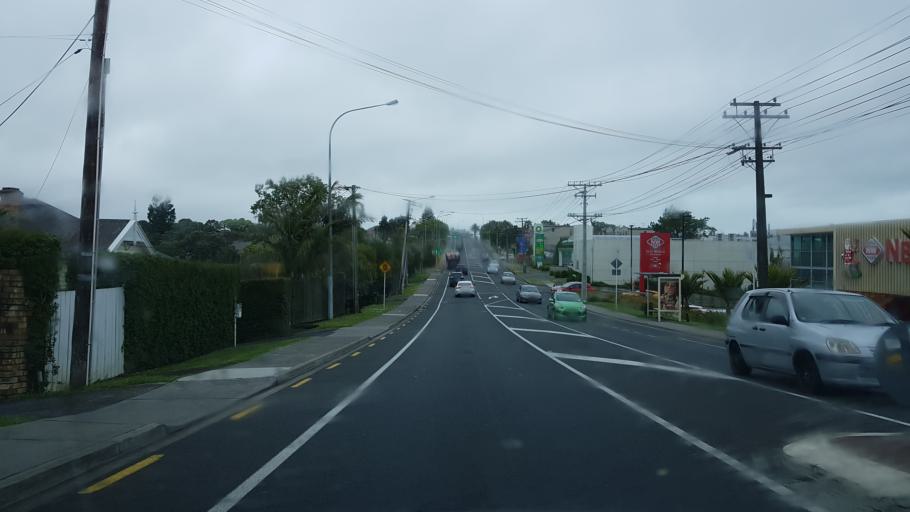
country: NZ
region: Auckland
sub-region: Auckland
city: North Shore
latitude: -36.8108
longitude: 174.7109
